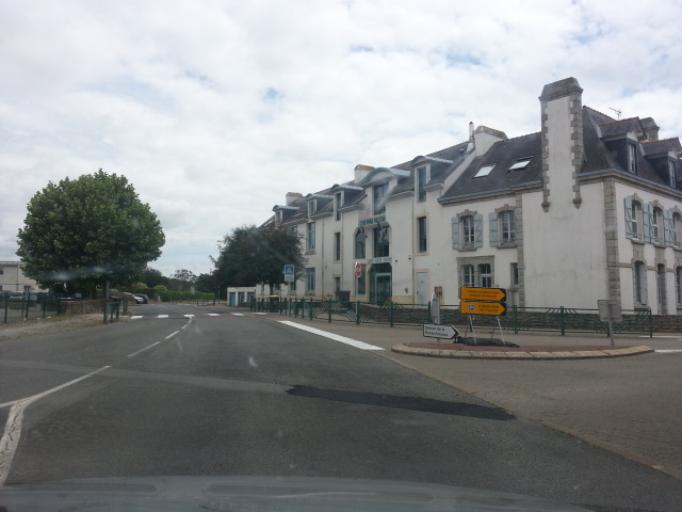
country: FR
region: Brittany
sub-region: Departement du Finistere
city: Tregunc
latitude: 47.8562
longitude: -3.8493
